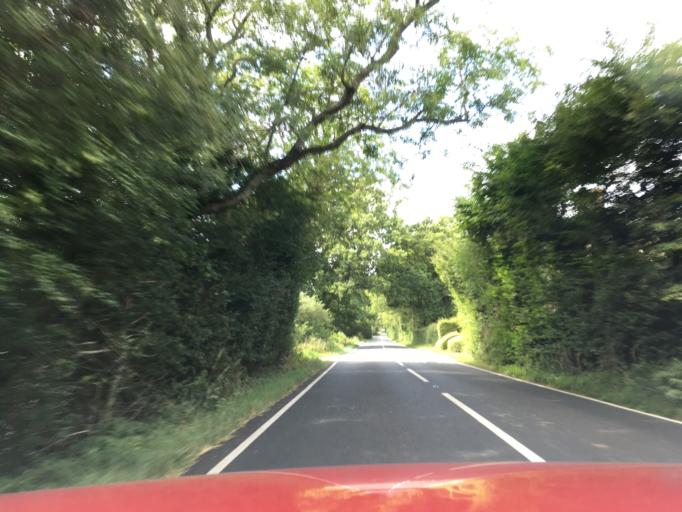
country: GB
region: England
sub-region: Kent
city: Edenbridge
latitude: 51.1283
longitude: 0.1128
